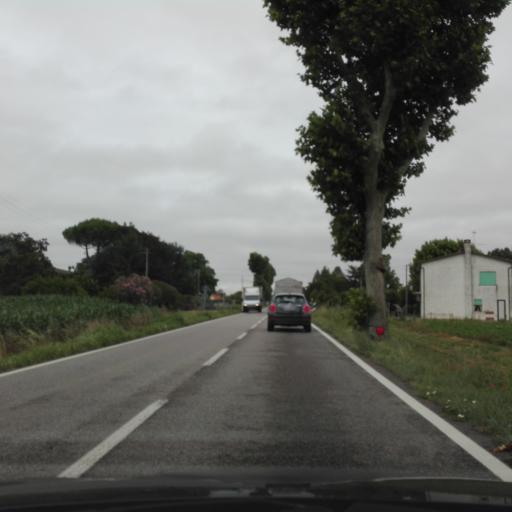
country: IT
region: Veneto
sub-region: Provincia di Rovigo
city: Lusia
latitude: 45.0755
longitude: 11.6614
